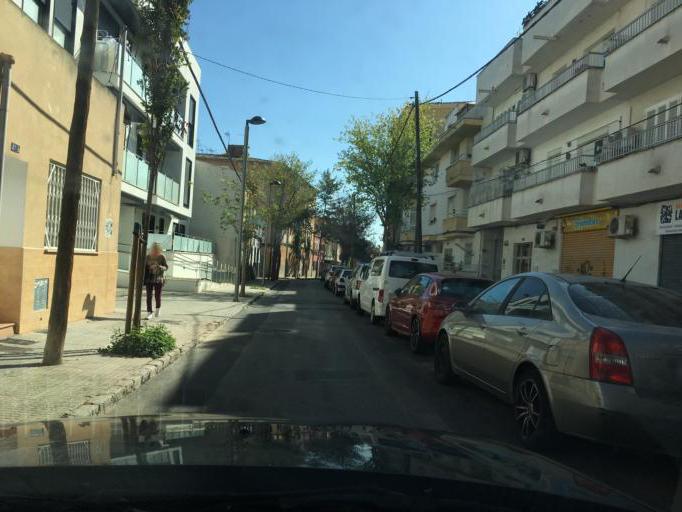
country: ES
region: Balearic Islands
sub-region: Illes Balears
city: Palma
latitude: 39.5842
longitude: 2.6761
